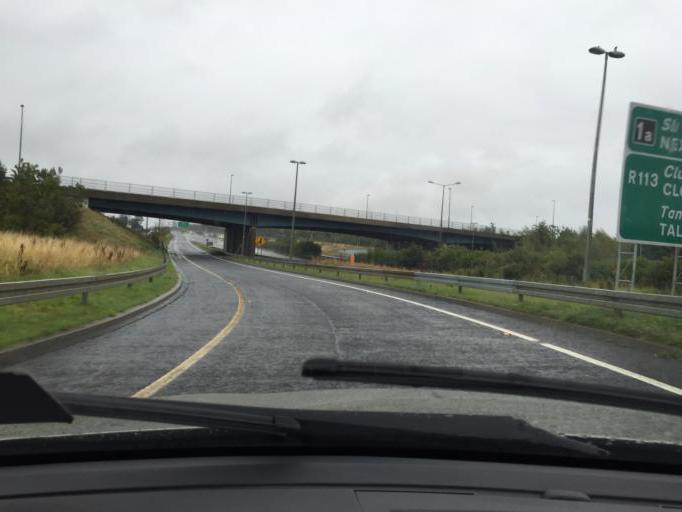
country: IE
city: Jobstown
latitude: 53.3023
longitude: -6.4198
